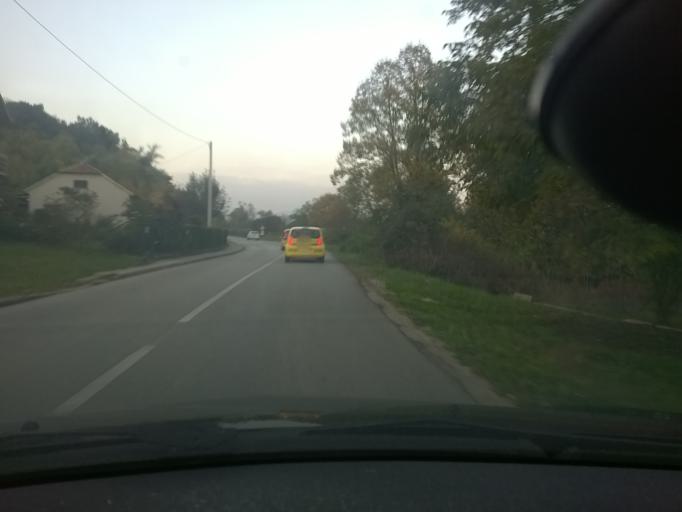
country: HR
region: Krapinsko-Zagorska
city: Zabok
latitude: 46.0448
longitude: 15.9101
